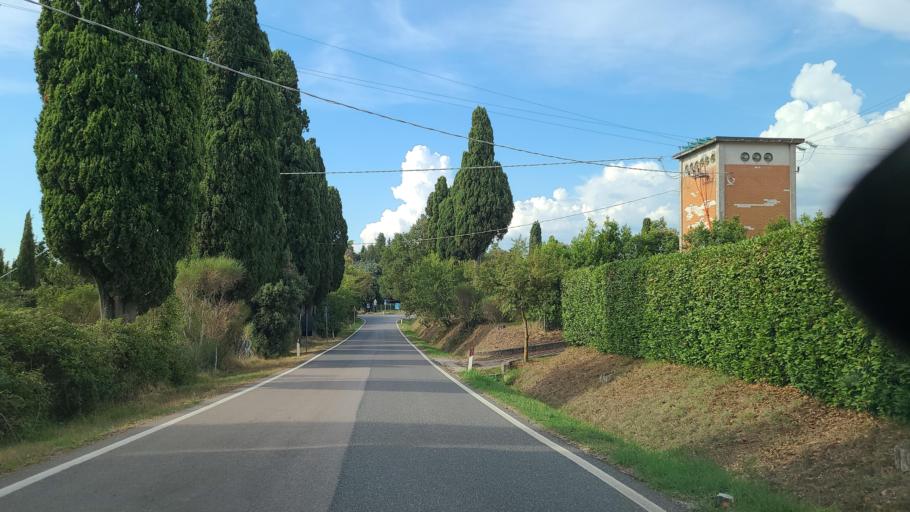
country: IT
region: Tuscany
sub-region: Province of Florence
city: Gambassi Terme
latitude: 43.4796
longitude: 10.9542
